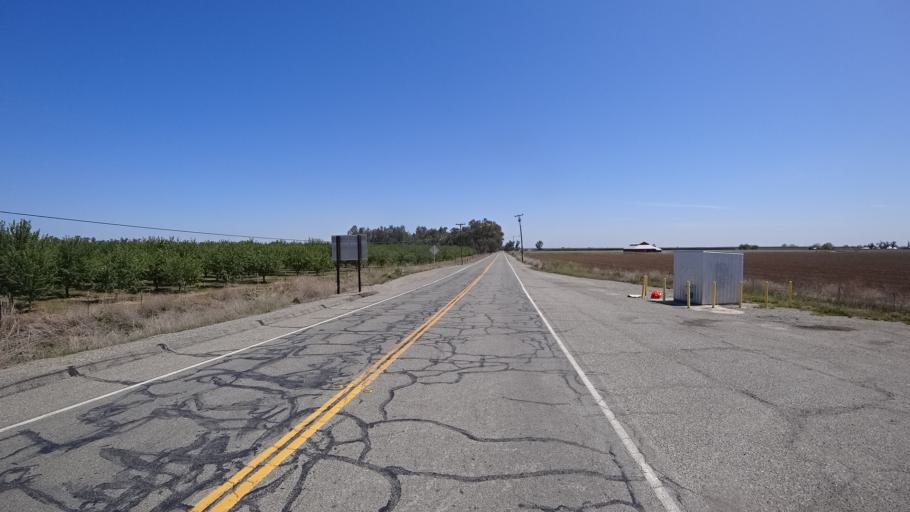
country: US
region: California
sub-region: Glenn County
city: Willows
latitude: 39.5824
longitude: -122.2084
